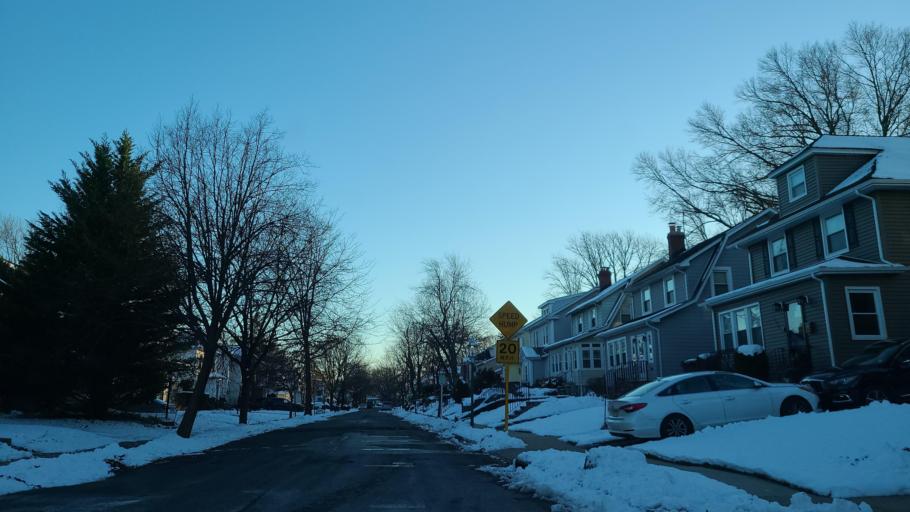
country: US
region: New Jersey
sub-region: Essex County
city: Irvington
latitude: 40.7490
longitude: -74.2364
